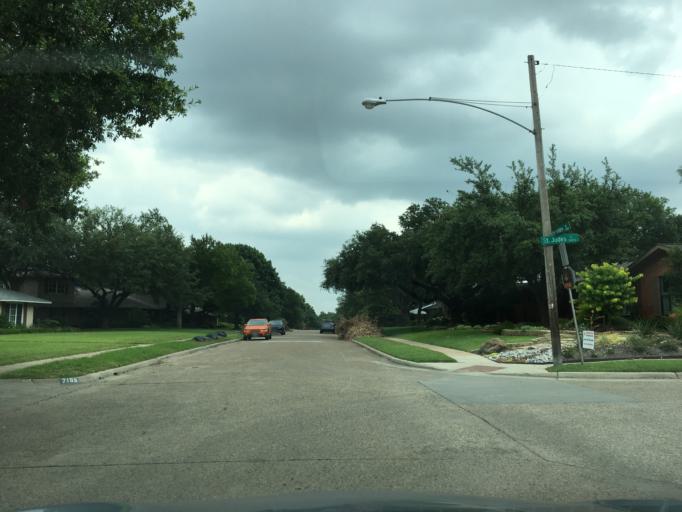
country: US
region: Texas
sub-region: Dallas County
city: University Park
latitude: 32.9049
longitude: -96.7853
